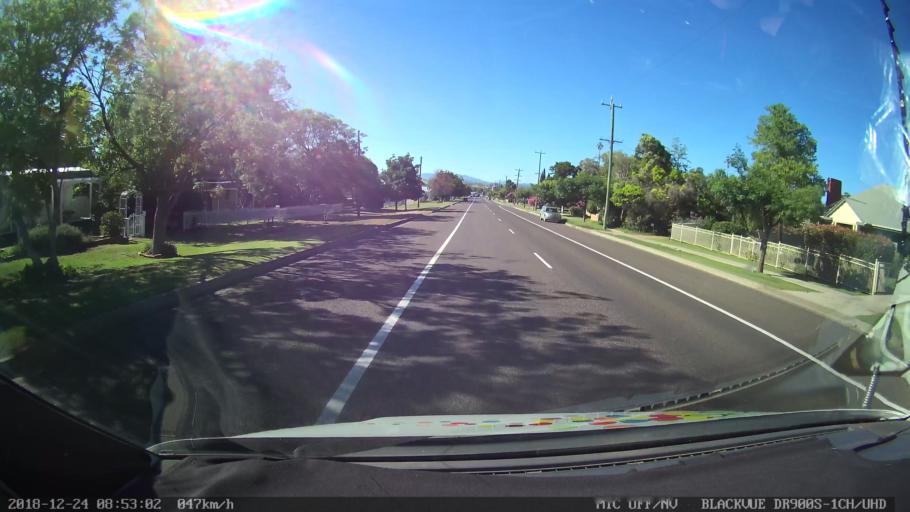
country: AU
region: New South Wales
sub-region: Liverpool Plains
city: Quirindi
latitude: -31.4956
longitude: 150.6809
